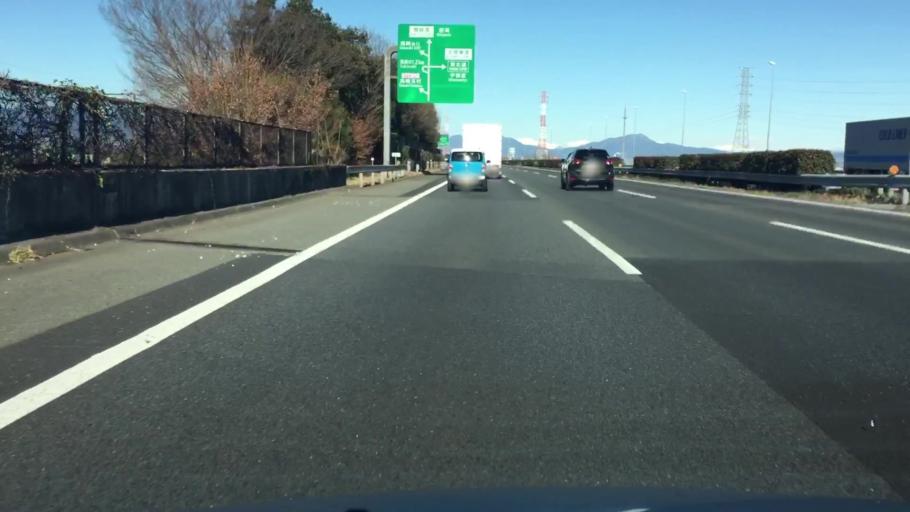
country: JP
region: Gunma
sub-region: Sawa-gun
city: Tamamura
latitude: 36.3036
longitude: 139.0936
